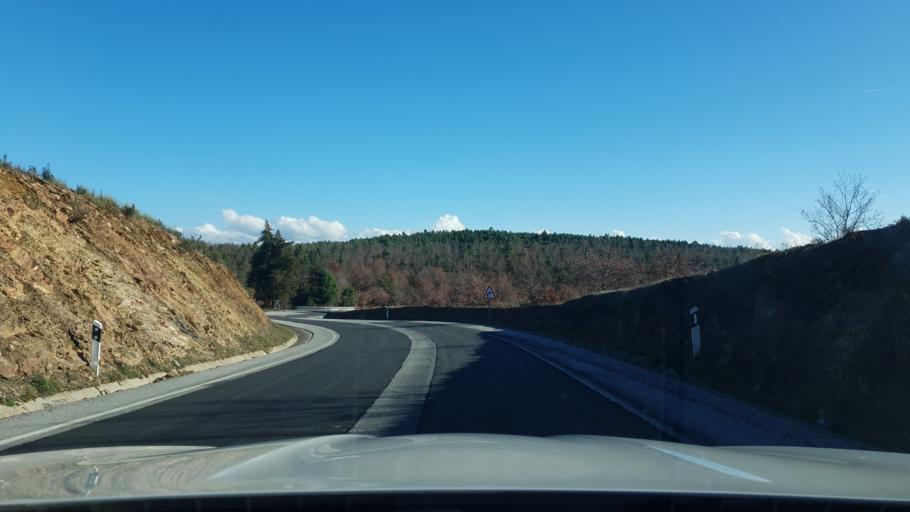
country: PT
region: Braganca
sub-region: Freixo de Espada A Cinta
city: Freixo de Espada a Cinta
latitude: 41.1389
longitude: -6.8067
